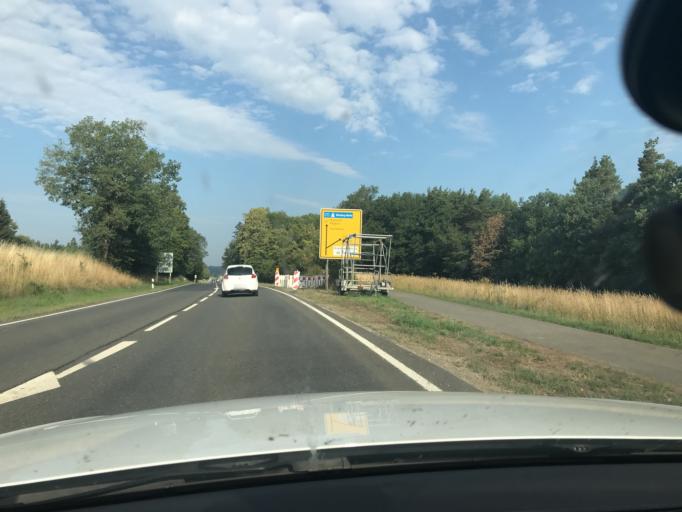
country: DE
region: Bavaria
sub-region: Upper Palatinate
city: Auerbach
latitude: 49.6986
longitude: 11.6151
